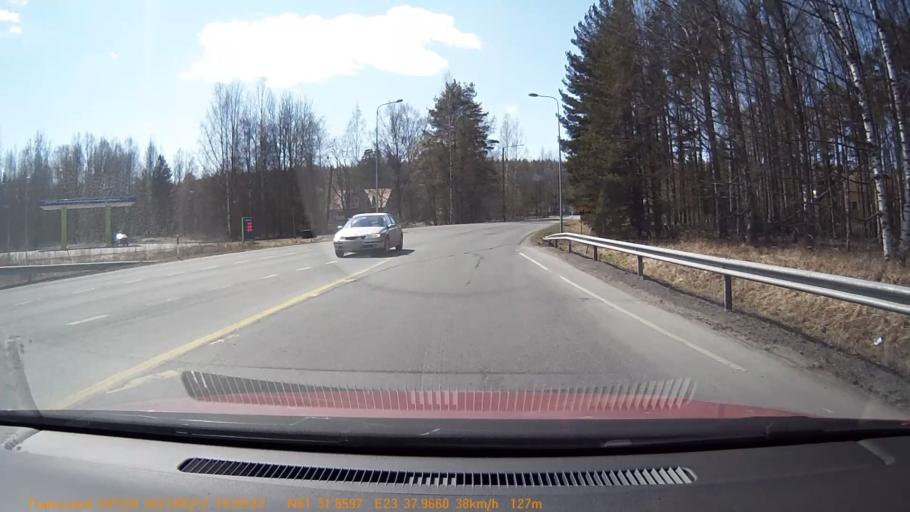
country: FI
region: Pirkanmaa
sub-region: Tampere
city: Yloejaervi
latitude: 61.5311
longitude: 23.6331
